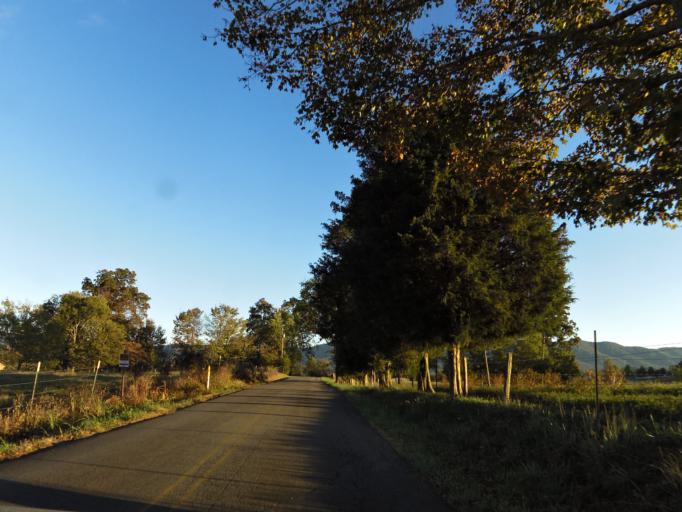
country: US
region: Tennessee
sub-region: Blount County
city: Wildwood
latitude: 35.8193
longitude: -83.7829
